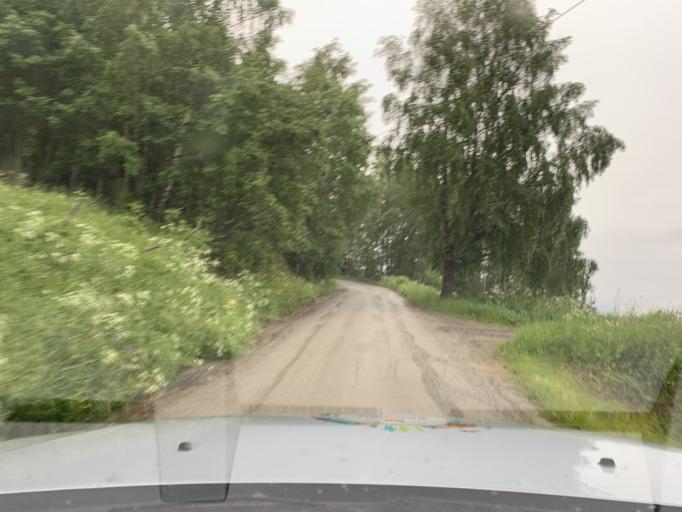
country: NO
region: Oppland
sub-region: Oyer
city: Tretten
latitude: 61.3894
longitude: 10.2580
